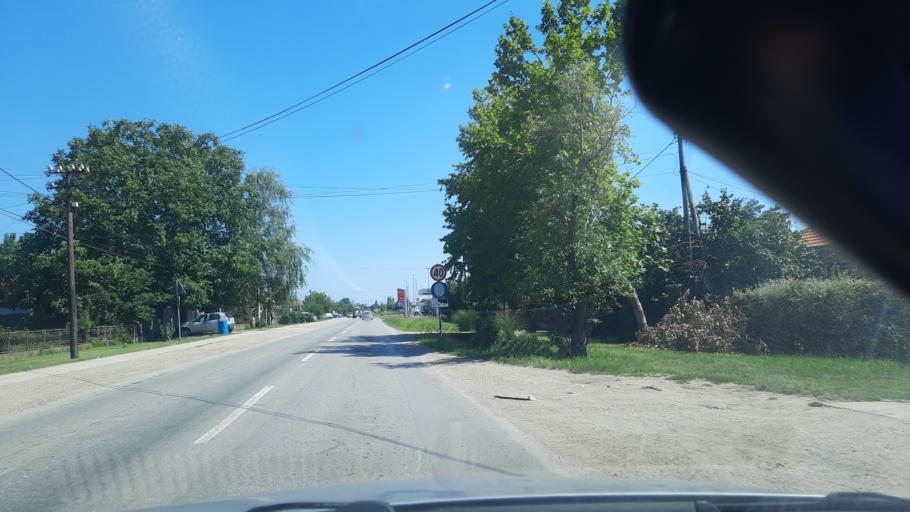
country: RS
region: Central Serbia
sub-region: Podunavski Okrug
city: Smederevo
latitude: 44.5974
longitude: 20.9900
